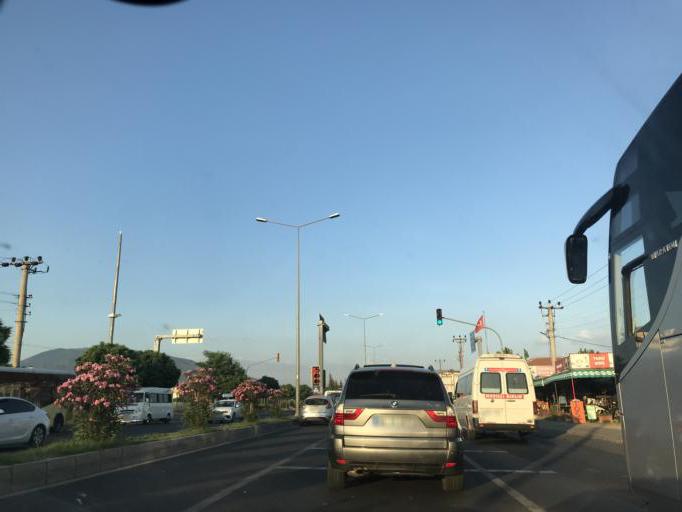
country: TR
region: Aydin
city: Nazilli
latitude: 37.9141
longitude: 28.3520
